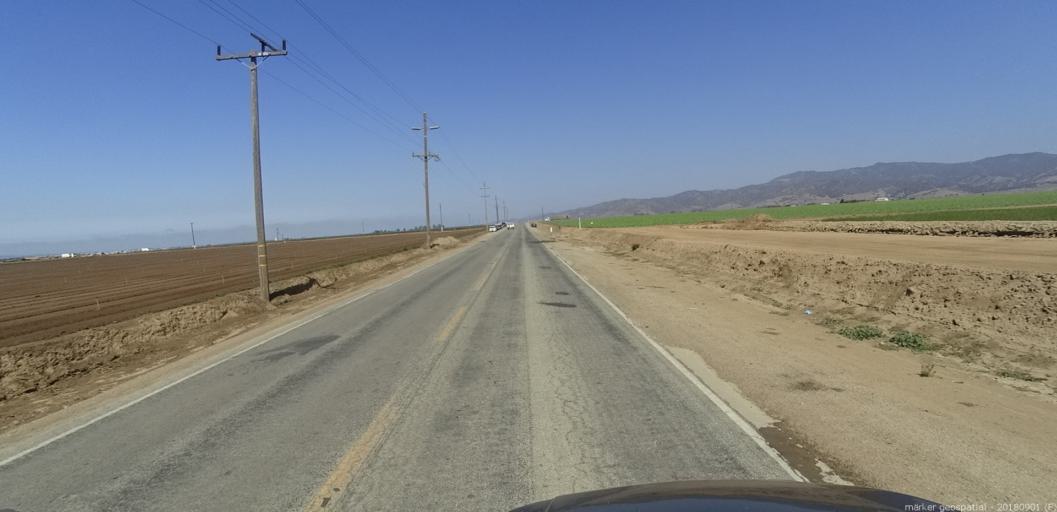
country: US
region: California
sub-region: Monterey County
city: Chualar
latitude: 36.5871
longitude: -121.5009
